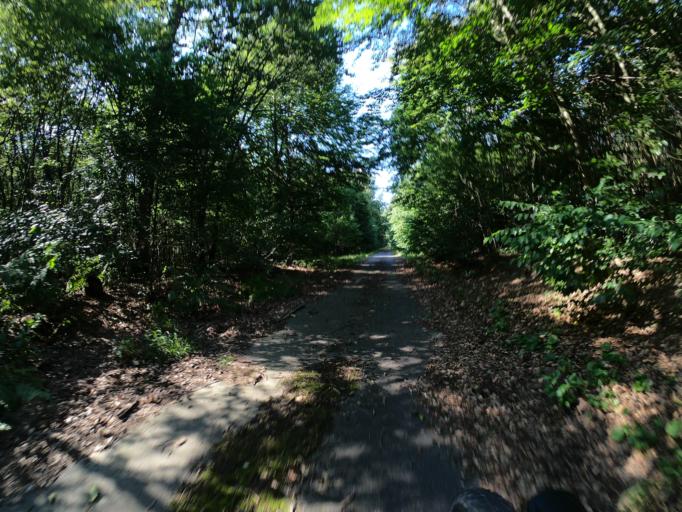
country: DE
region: Hesse
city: Morfelden-Walldorf
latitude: 49.9906
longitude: 8.6089
